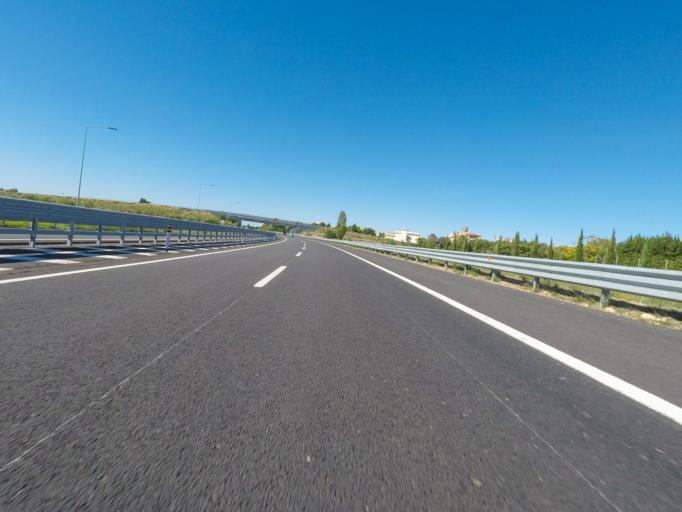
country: IT
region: Latium
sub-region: Provincia di Viterbo
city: Tarquinia
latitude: 42.2396
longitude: 11.7587
